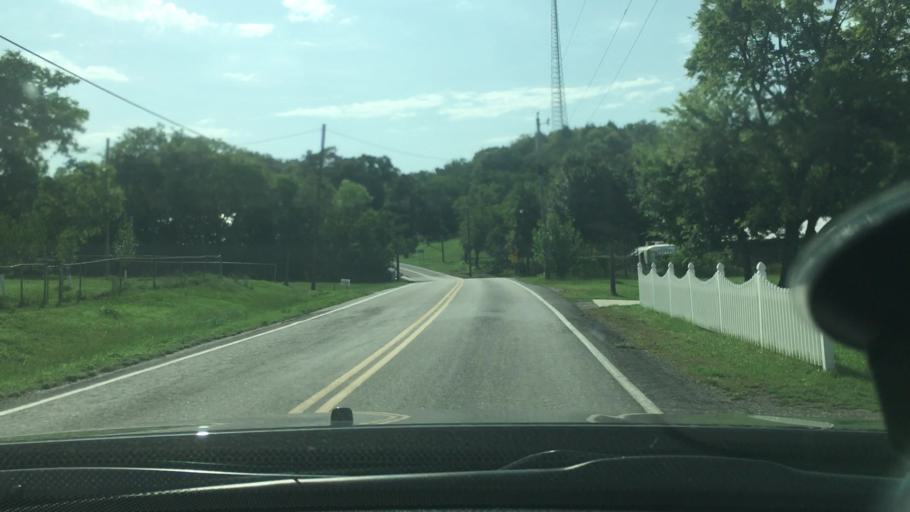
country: US
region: Oklahoma
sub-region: Atoka County
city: Atoka
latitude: 34.4684
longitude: -96.0515
